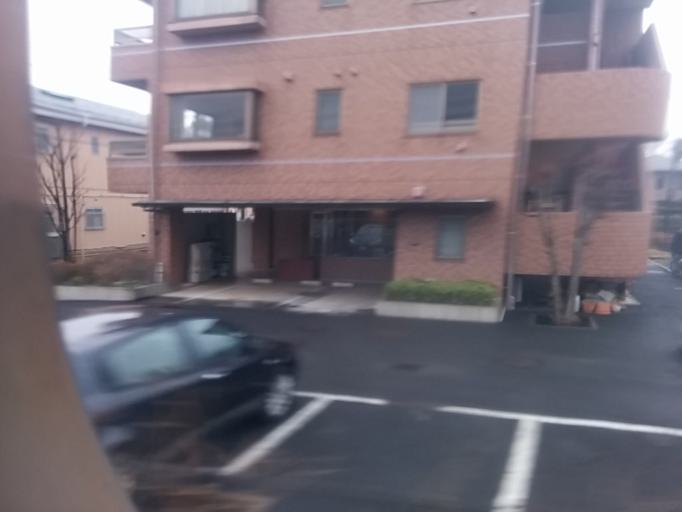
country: JP
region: Tokyo
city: Chofugaoka
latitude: 35.6634
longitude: 139.5153
